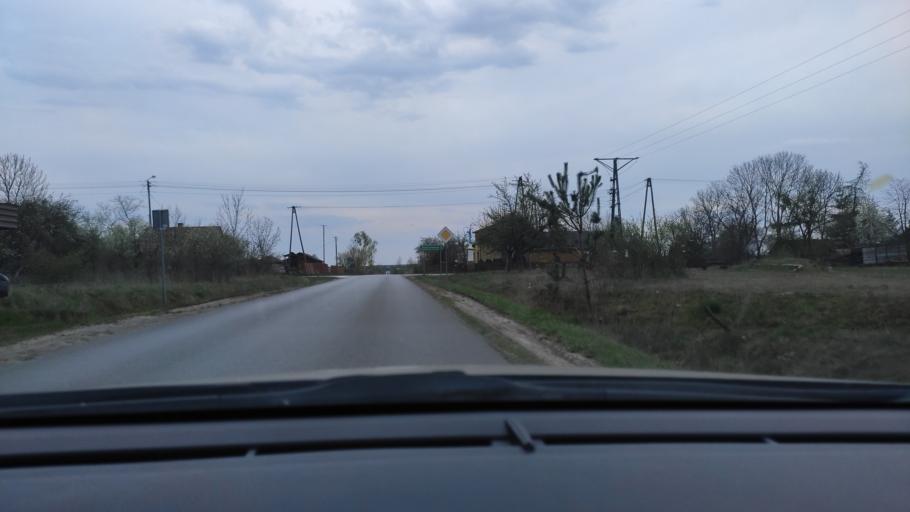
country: PL
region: Masovian Voivodeship
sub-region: Powiat radomski
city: Pionki
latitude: 51.5686
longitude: 21.3652
